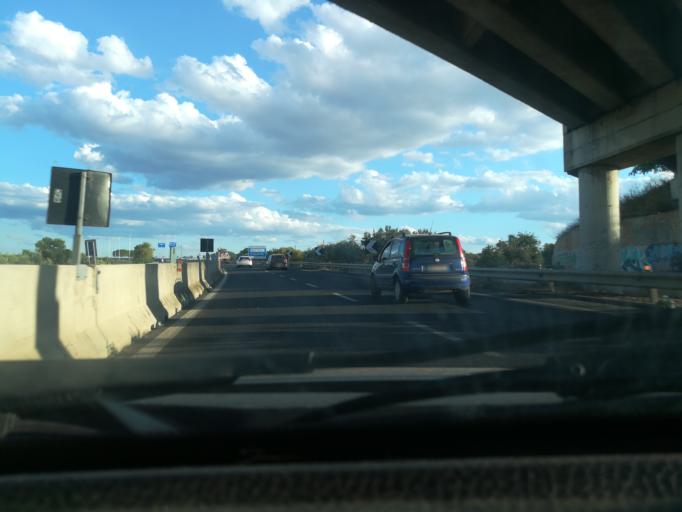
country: IT
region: Apulia
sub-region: Provincia di Bari
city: Mola di Bari
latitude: 41.0545
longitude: 17.0698
